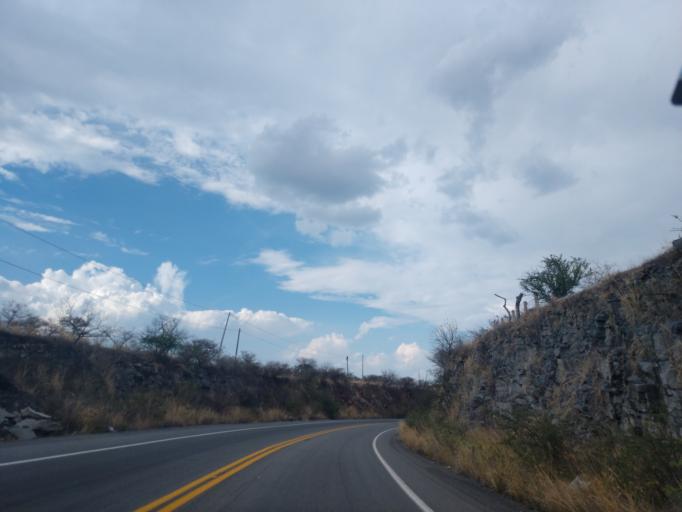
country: MX
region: Jalisco
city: La Manzanilla de la Paz
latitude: 20.1117
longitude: -103.1660
